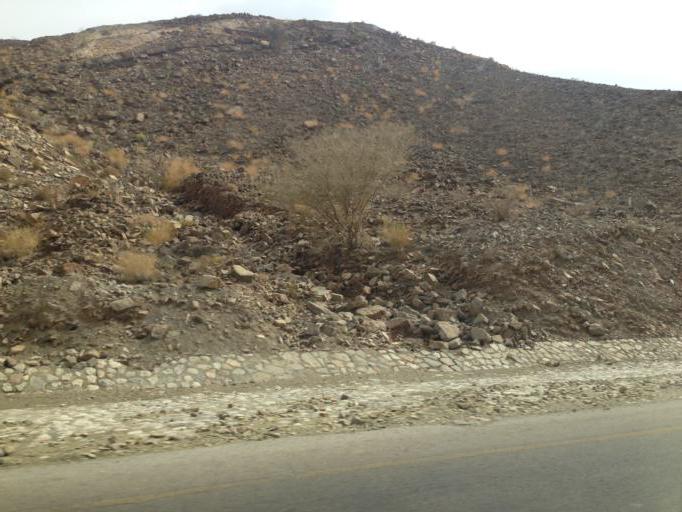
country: OM
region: Ash Sharqiyah
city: Badiyah
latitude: 22.5317
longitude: 58.9629
